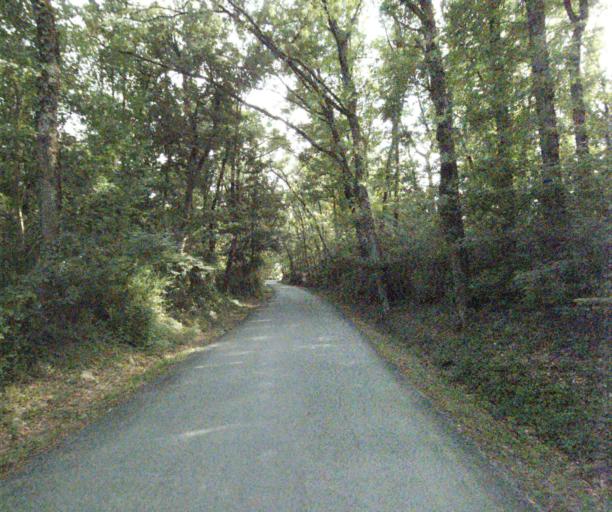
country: FR
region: Midi-Pyrenees
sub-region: Departement du Tarn
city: Puylaurens
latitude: 43.5464
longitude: 2.0594
